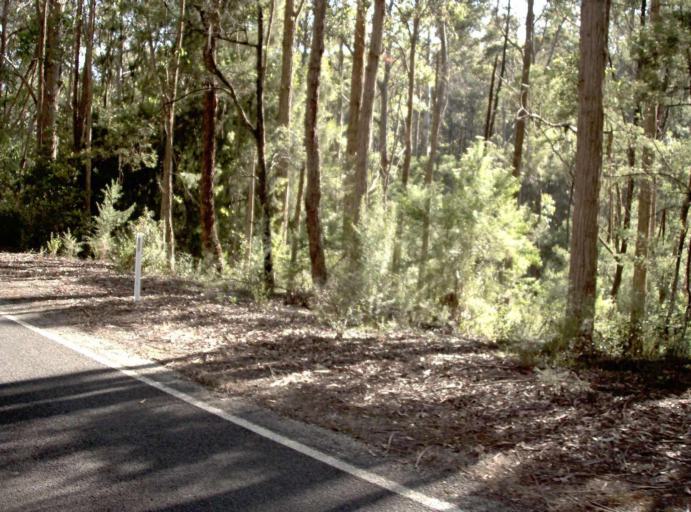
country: AU
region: Victoria
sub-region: East Gippsland
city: Lakes Entrance
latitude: -37.6476
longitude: 148.4817
